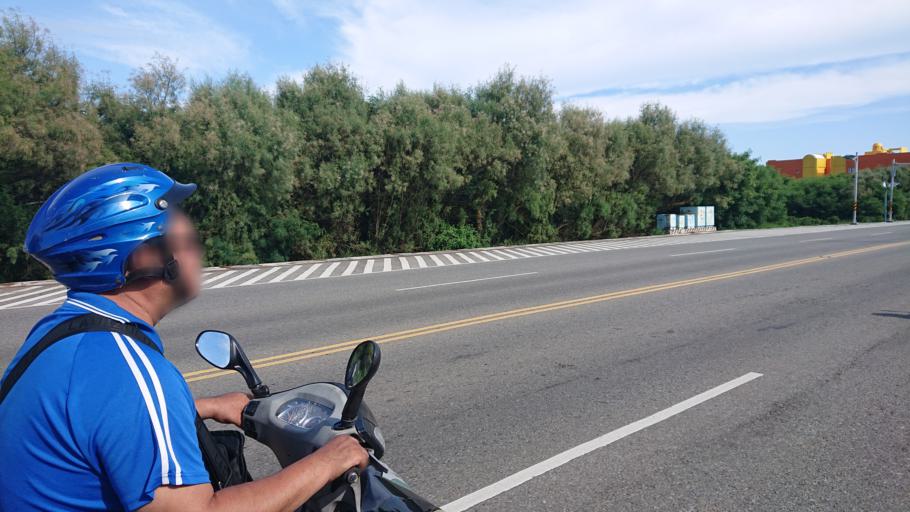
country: TW
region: Taiwan
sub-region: Penghu
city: Ma-kung
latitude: 23.5343
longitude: 119.6026
